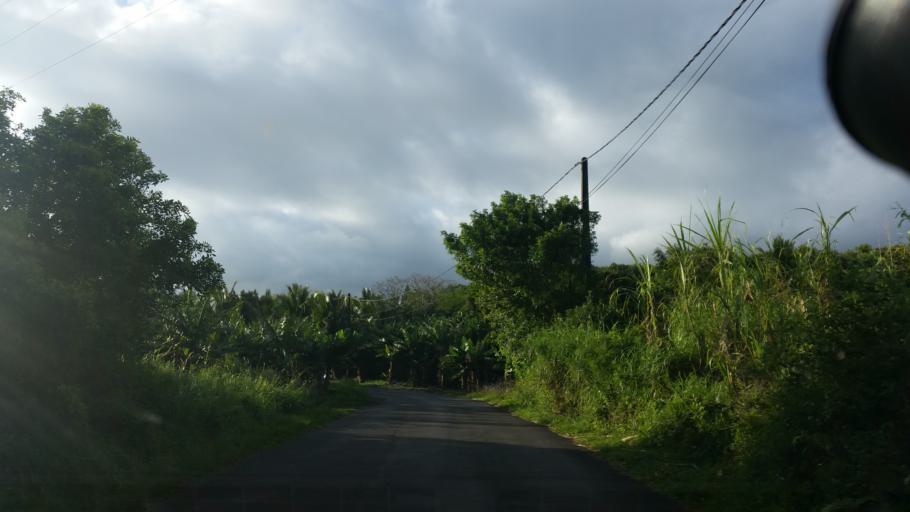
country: RE
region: Reunion
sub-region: Reunion
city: Saint-Joseph
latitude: -21.3773
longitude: 55.6697
